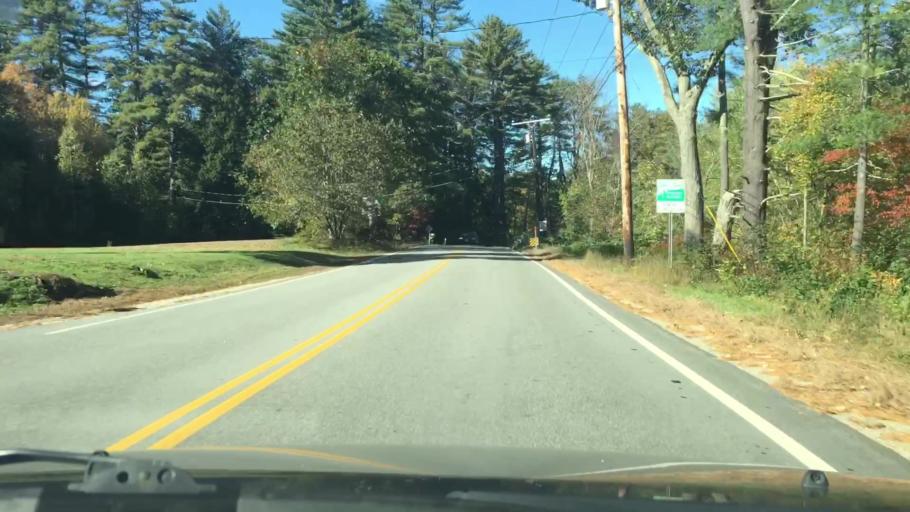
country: US
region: New Hampshire
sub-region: Cheshire County
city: Swanzey
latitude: 42.8472
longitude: -72.2792
